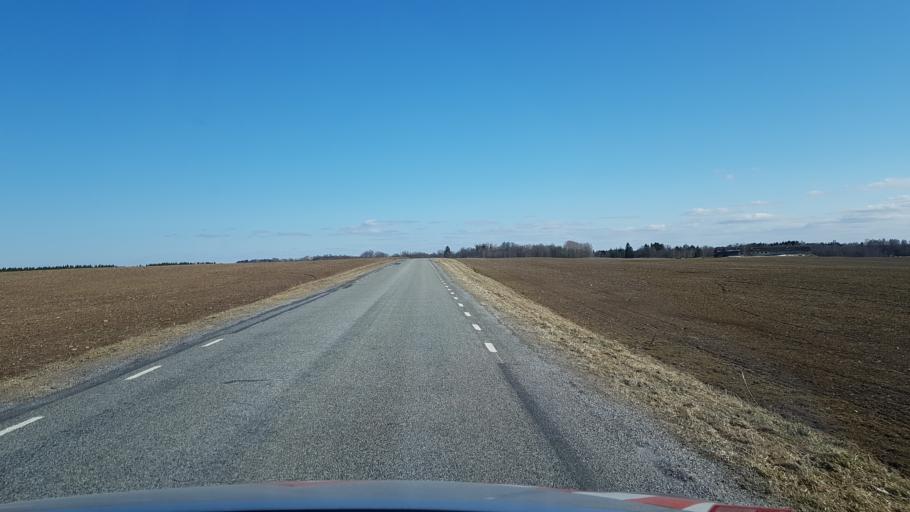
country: EE
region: Laeaene-Virumaa
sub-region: Kadrina vald
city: Kadrina
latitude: 59.3809
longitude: 26.0295
